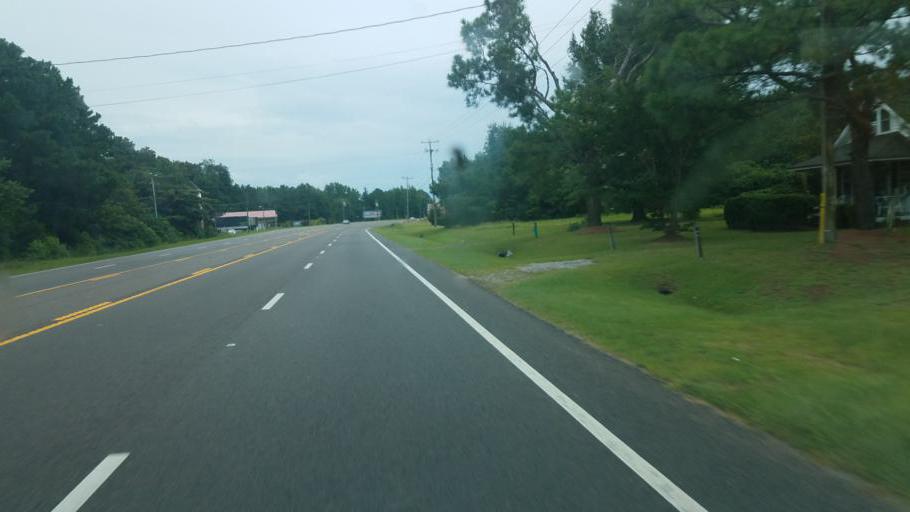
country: US
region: North Carolina
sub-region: Dare County
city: Southern Shores
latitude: 36.1350
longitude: -75.8391
